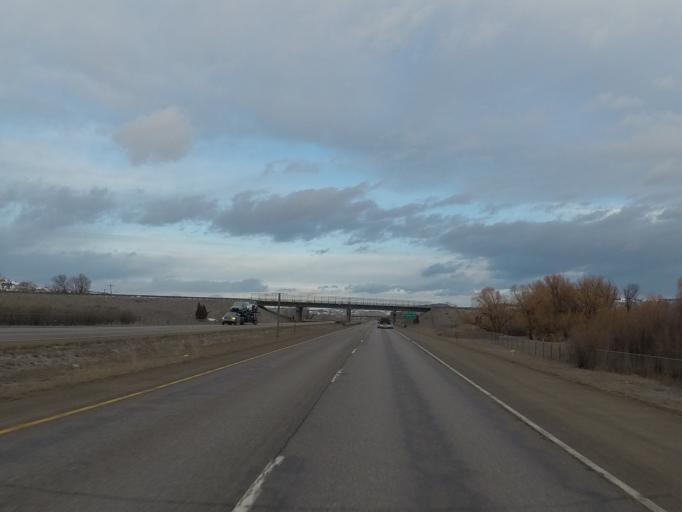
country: US
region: Montana
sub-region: Silver Bow County
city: Butte
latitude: 45.9874
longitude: -112.5184
